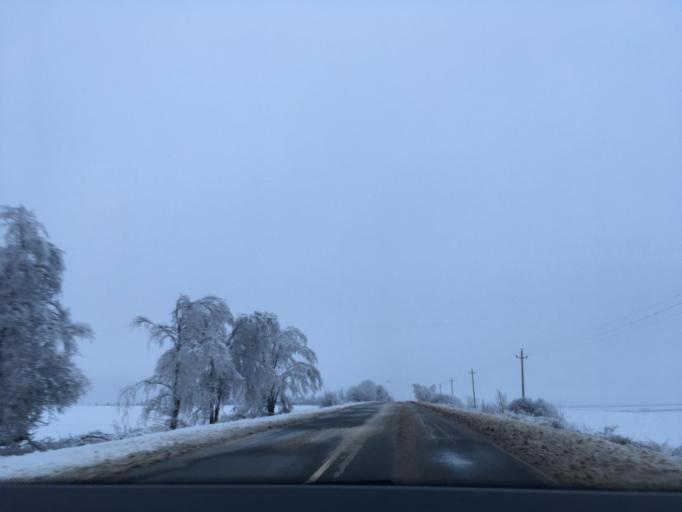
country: RU
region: Voronezj
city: Verkhniy Mamon
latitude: 50.0236
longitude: 40.0776
